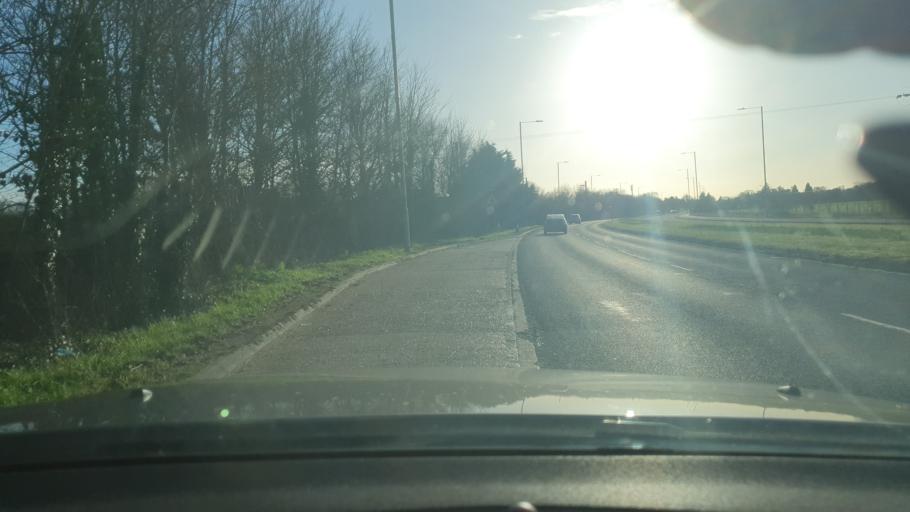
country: GB
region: England
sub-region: Wokingham
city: Charvil
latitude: 51.4718
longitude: -0.8949
